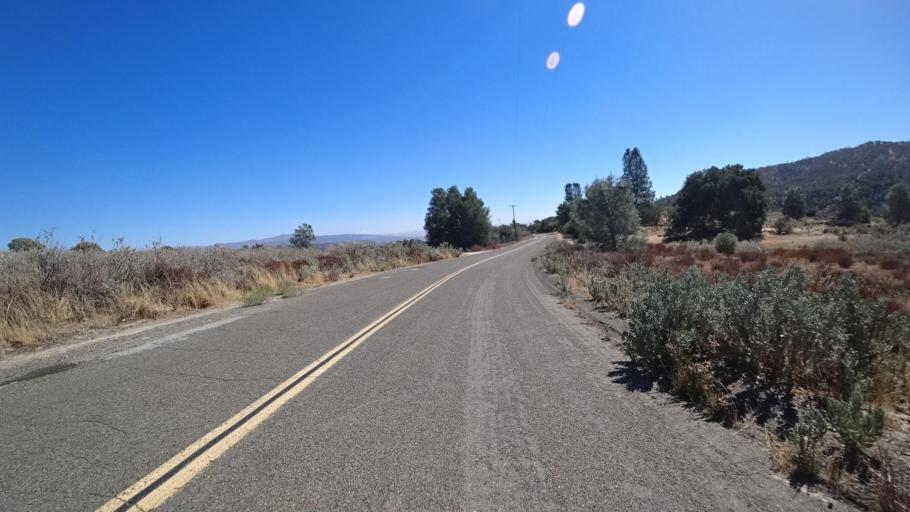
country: US
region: California
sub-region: San Luis Obispo County
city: San Miguel
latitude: 35.9206
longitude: -120.5242
